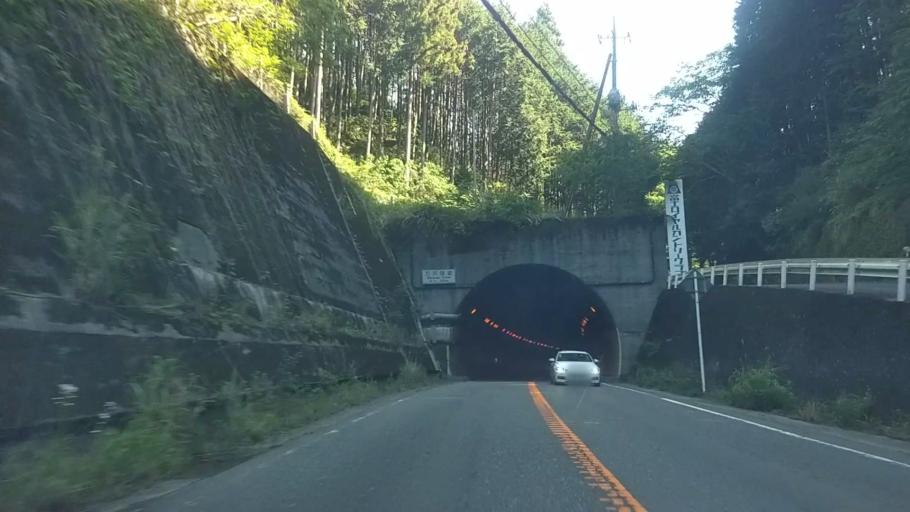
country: JP
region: Shizuoka
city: Fujinomiya
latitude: 35.2061
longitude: 138.5158
